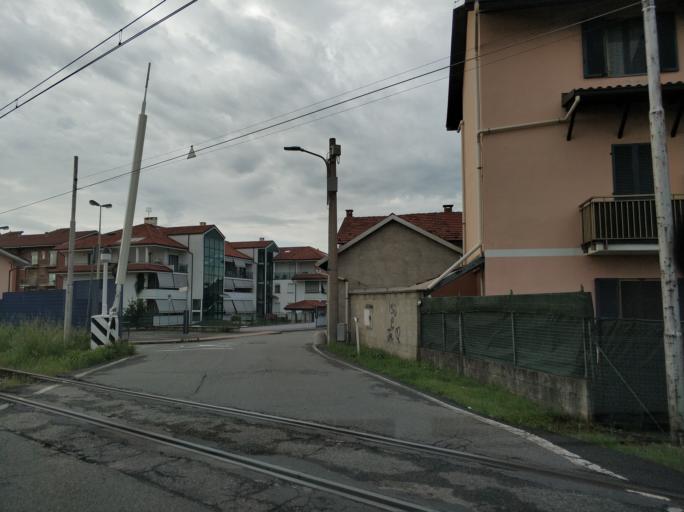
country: IT
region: Piedmont
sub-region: Provincia di Torino
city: Cirie
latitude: 45.2272
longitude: 7.6084
